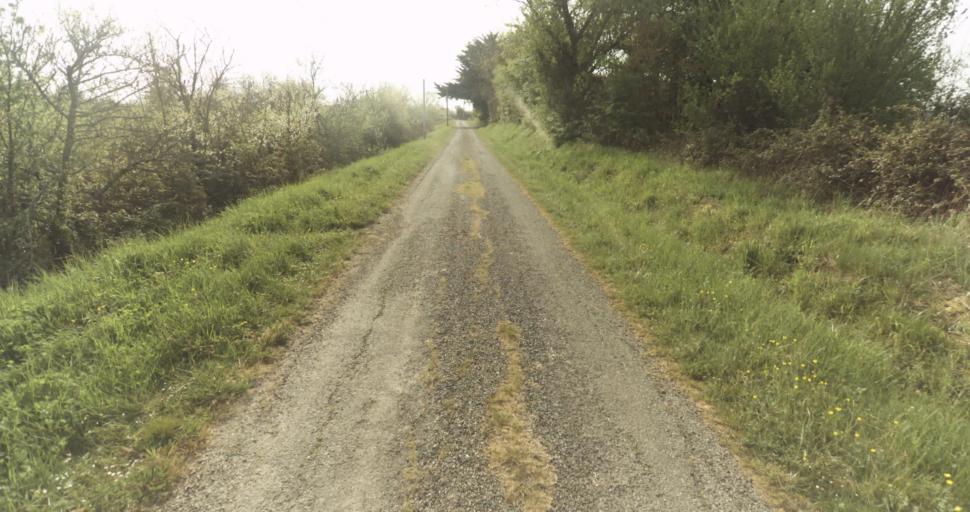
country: FR
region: Midi-Pyrenees
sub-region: Departement du Tarn-et-Garonne
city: Moissac
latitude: 44.1573
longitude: 1.0400
